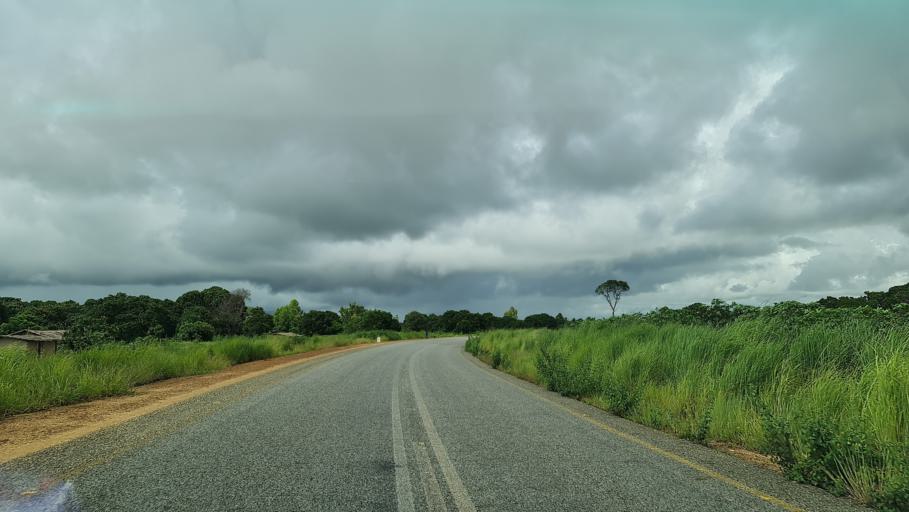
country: MZ
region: Nampula
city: Nampula
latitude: -15.0519
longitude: 38.4214
